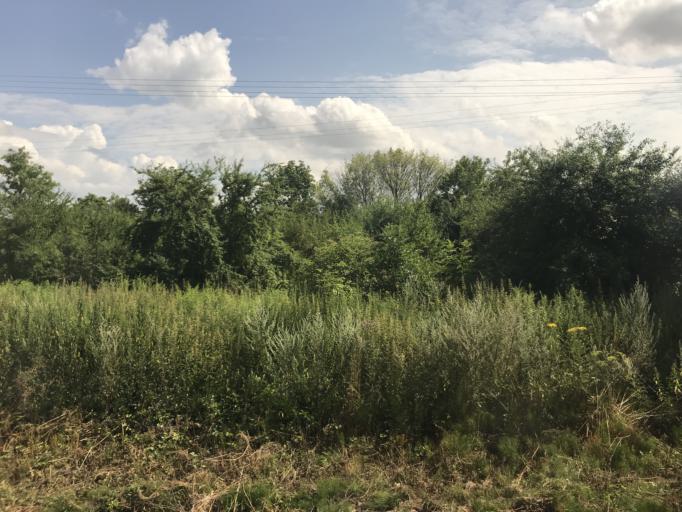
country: PL
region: Kujawsko-Pomorskie
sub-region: Powiat inowroclawski
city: Zlotniki Kujawskie
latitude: 52.9025
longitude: 18.1487
